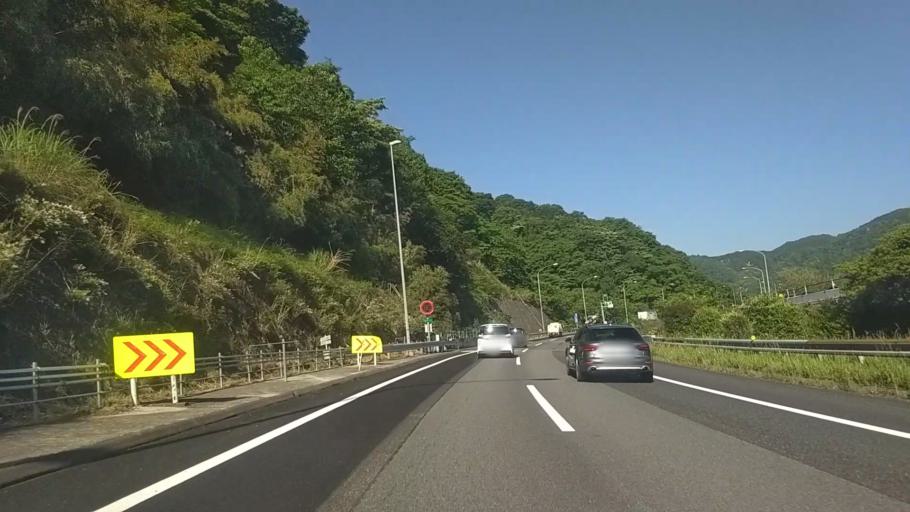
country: JP
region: Shizuoka
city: Gotemba
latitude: 35.3689
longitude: 139.0332
